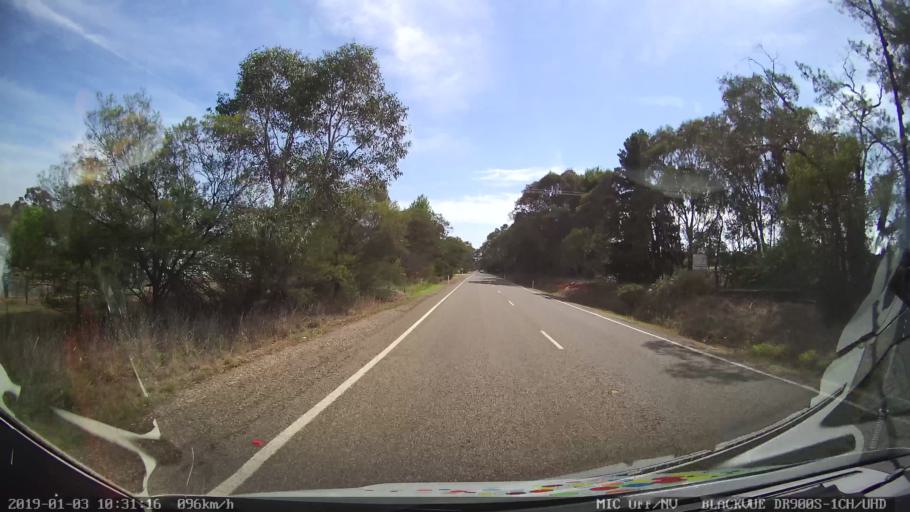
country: AU
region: New South Wales
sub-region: Young
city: Young
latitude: -34.3522
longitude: 148.2756
